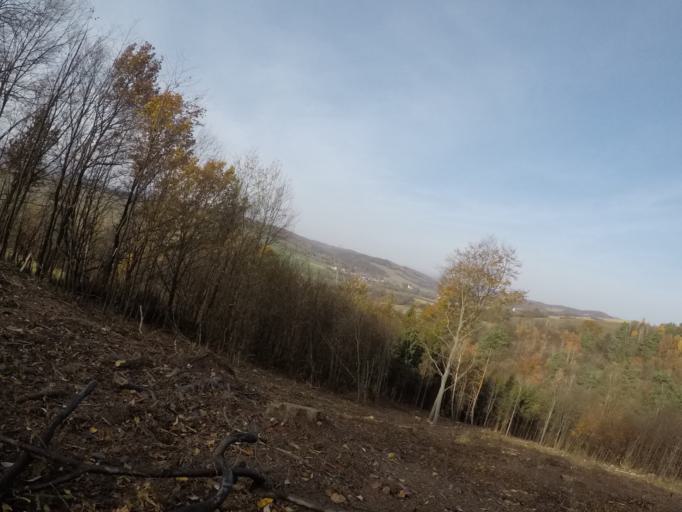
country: SK
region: Presovsky
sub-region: Okres Presov
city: Presov
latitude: 48.9157
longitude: 21.2083
